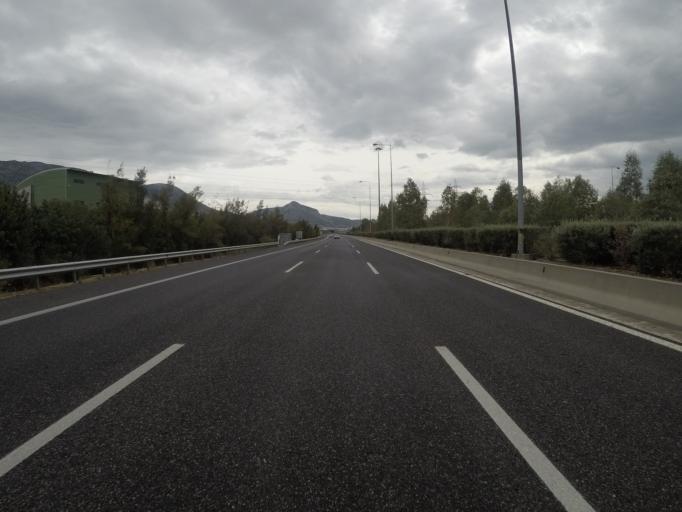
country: GR
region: Attica
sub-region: Nomarchia Dytikis Attikis
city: Aspropyrgos
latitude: 38.0947
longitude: 23.5781
